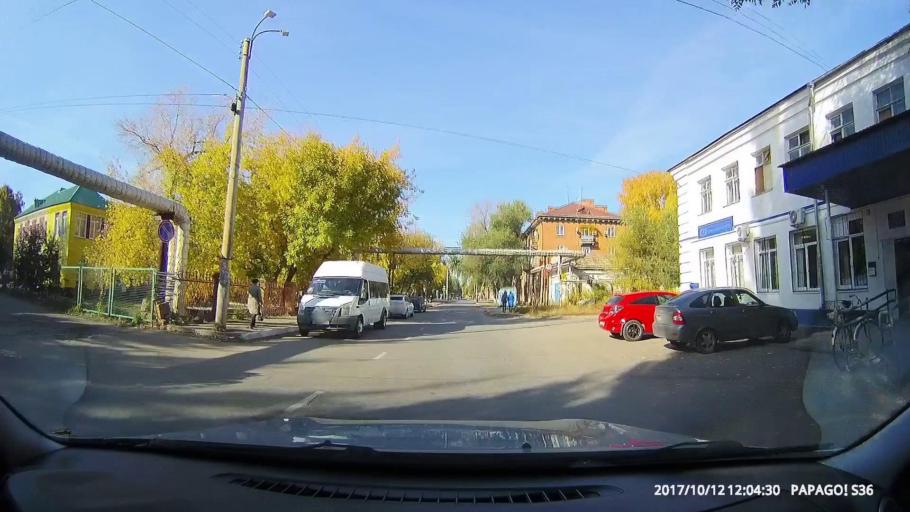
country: RU
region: Samara
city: Chapayevsk
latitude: 52.9782
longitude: 49.7157
